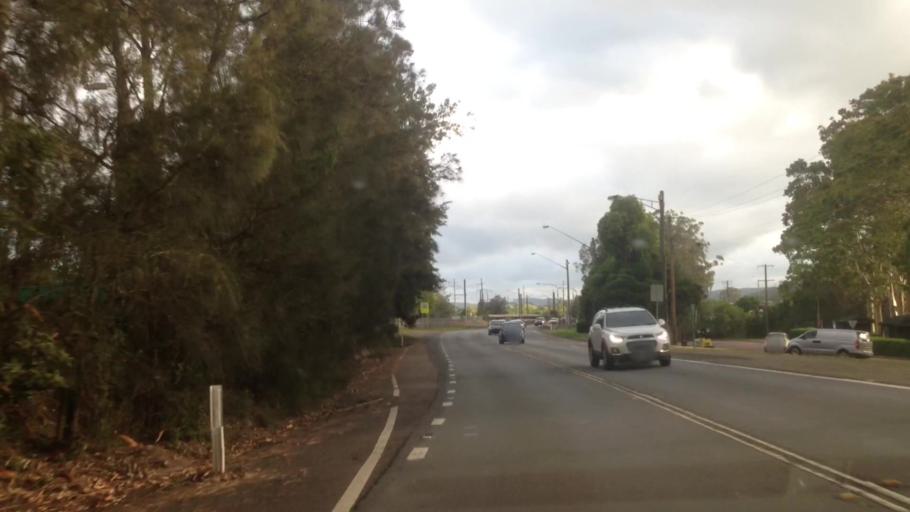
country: AU
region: New South Wales
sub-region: Wyong Shire
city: Chittaway Bay
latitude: -33.2886
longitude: 151.4241
